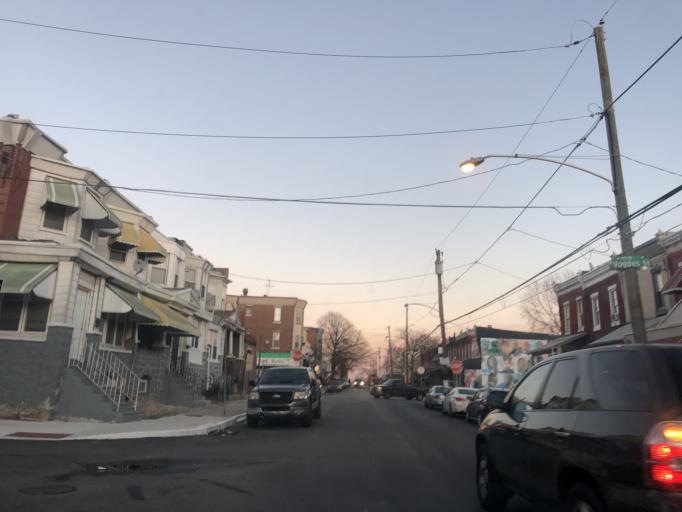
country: US
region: Pennsylvania
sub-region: Delaware County
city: Millbourne
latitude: 39.9737
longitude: -75.2318
